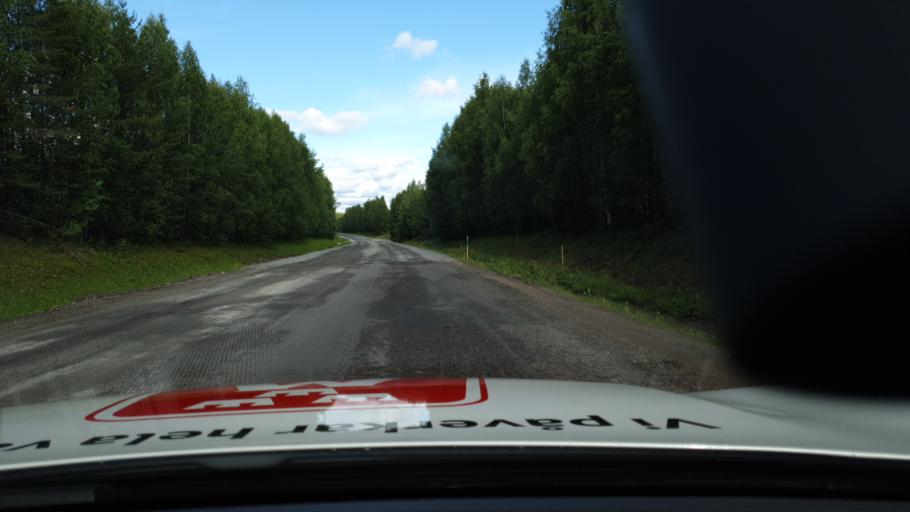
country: SE
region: Norrbotten
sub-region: Bodens Kommun
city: Boden
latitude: 65.8483
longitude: 21.5885
